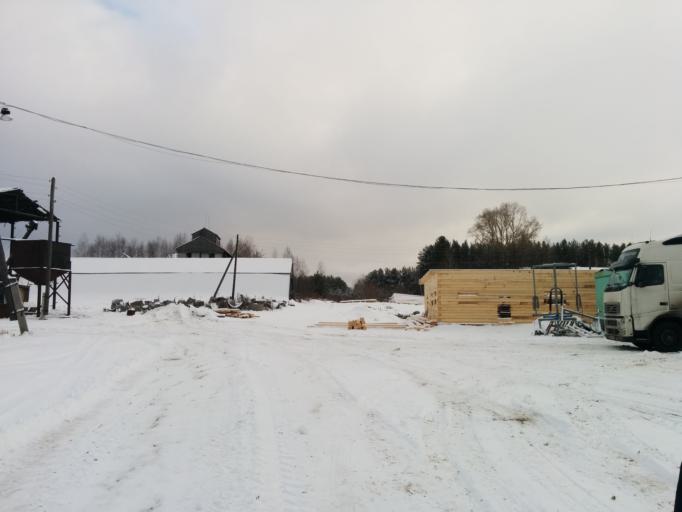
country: RU
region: Perm
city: Osa
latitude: 57.4758
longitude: 55.4868
